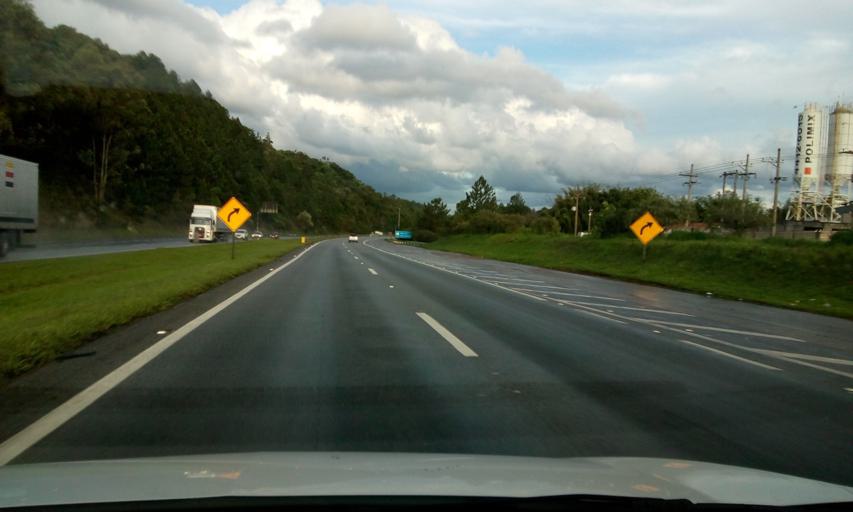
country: BR
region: Sao Paulo
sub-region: Atibaia
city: Atibaia
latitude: -23.0986
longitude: -46.5480
